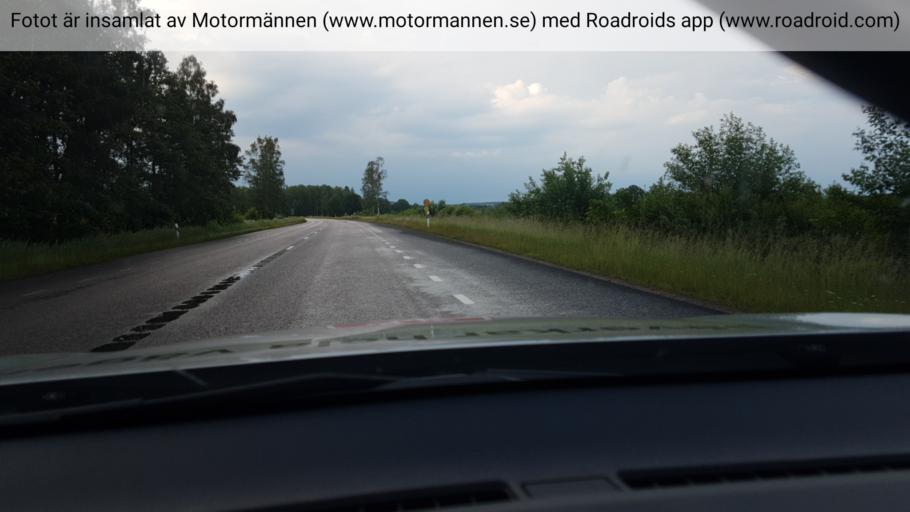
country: SE
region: Vaestra Goetaland
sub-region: Hjo Kommun
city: Hjo
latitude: 58.2892
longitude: 14.2614
